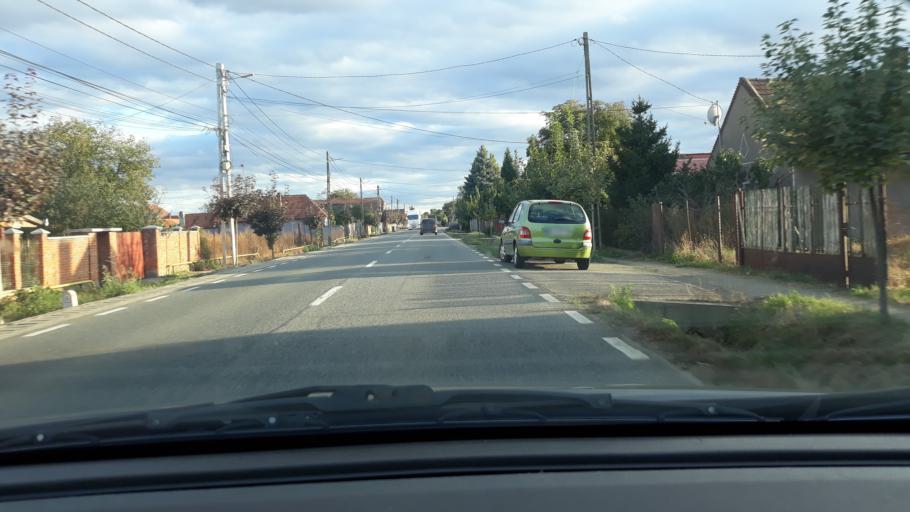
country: RO
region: Bihor
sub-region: Comuna Biharea
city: Biharea
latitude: 47.1677
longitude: 21.9220
